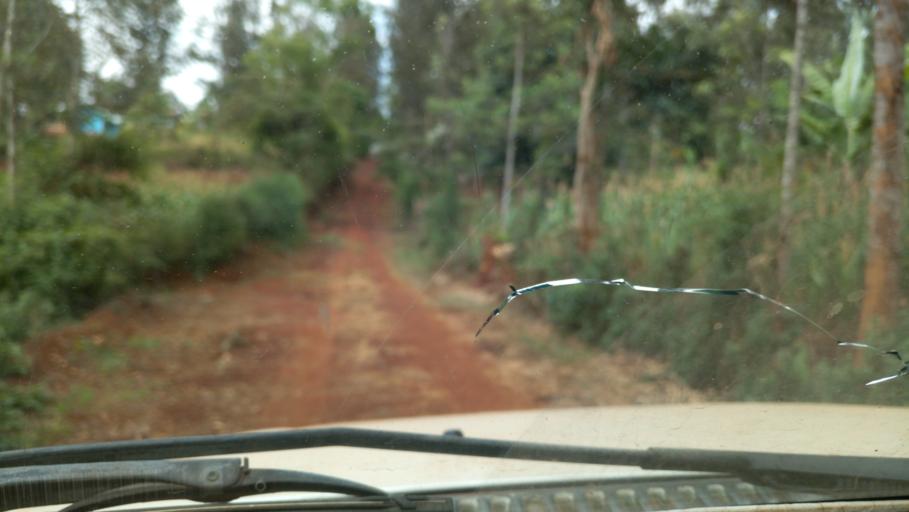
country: KE
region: Murang'a District
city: Maragua
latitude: -0.8531
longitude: 37.0590
